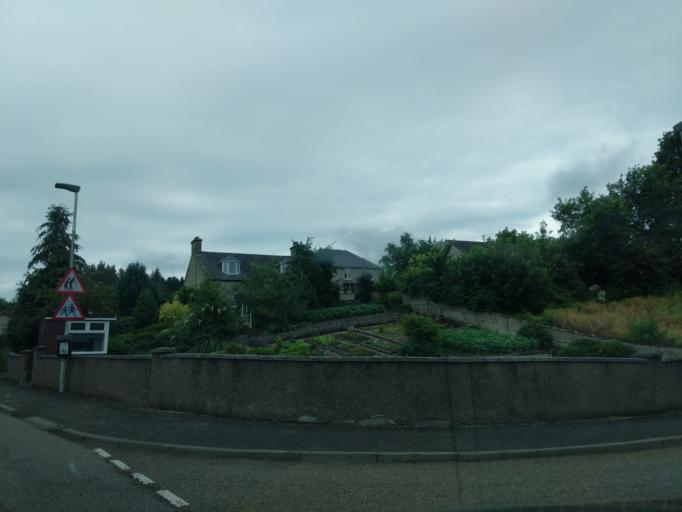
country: GB
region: Scotland
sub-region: Moray
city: Rothes
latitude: 57.4722
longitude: -3.2200
